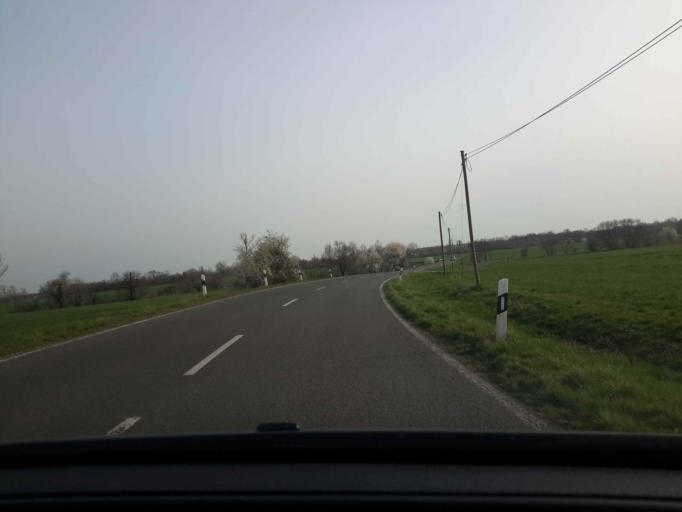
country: DE
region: Saxony
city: Rackwitz
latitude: 51.4432
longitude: 12.3544
